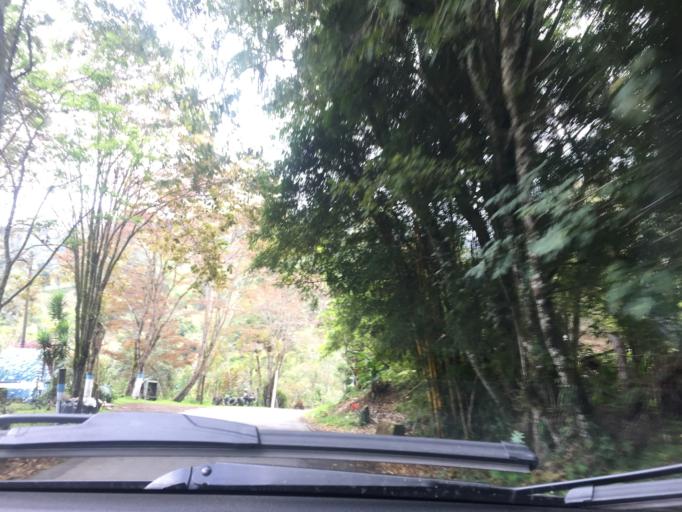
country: CO
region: Cundinamarca
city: Supata
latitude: 5.0545
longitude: -74.2382
